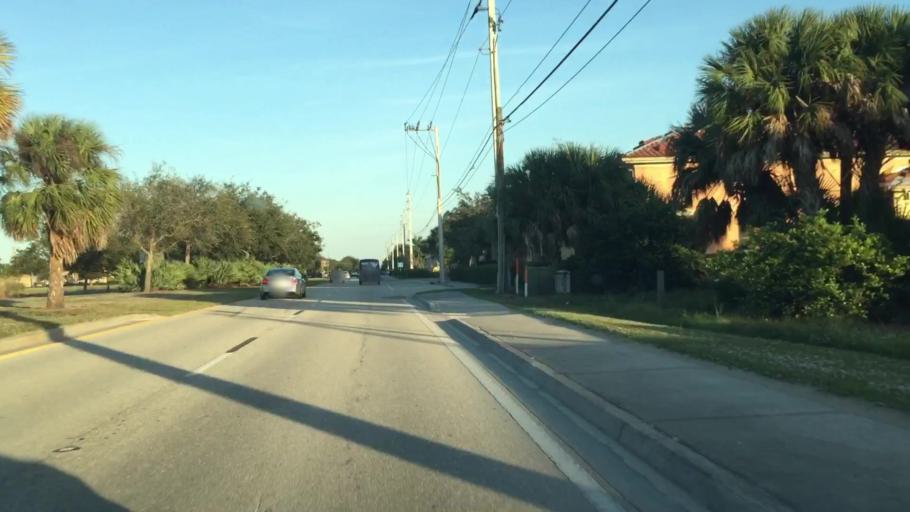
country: US
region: Florida
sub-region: Lee County
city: Estero
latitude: 26.4312
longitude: -81.8028
